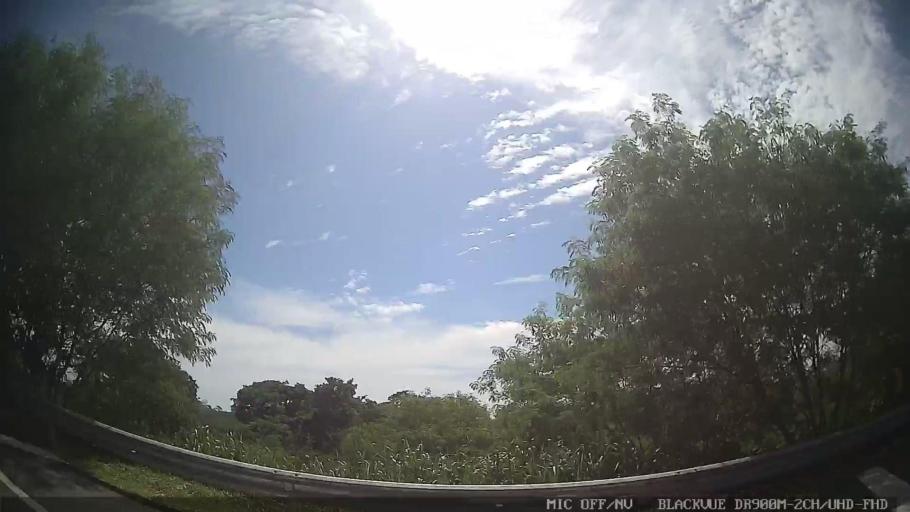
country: BR
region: Sao Paulo
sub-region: Porto Feliz
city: Porto Feliz
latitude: -23.2173
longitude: -47.5711
